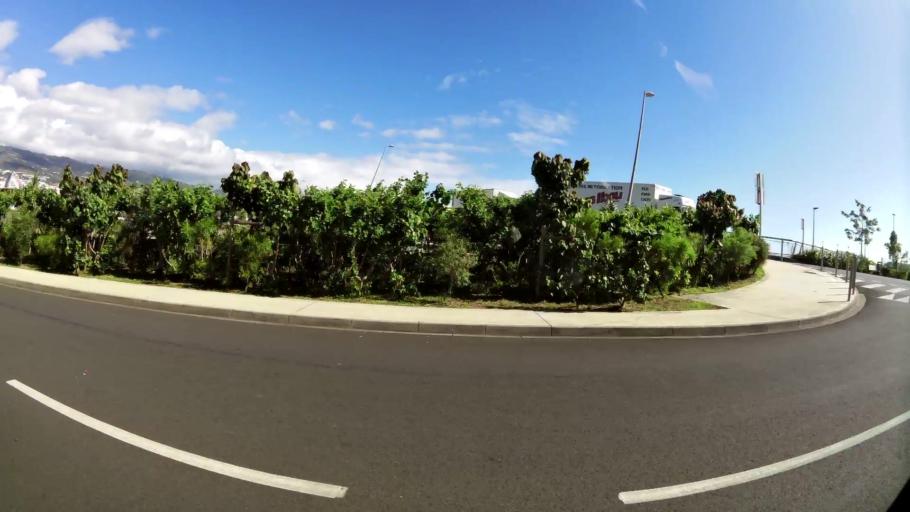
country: RE
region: Reunion
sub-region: Reunion
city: Sainte-Marie
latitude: -20.8944
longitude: 55.5001
